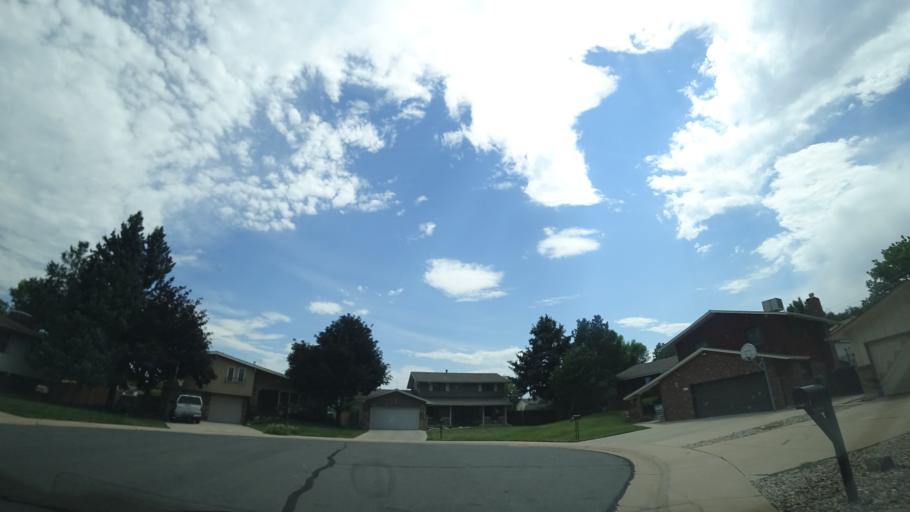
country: US
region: Colorado
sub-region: Jefferson County
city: Lakewood
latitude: 39.6963
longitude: -105.1066
